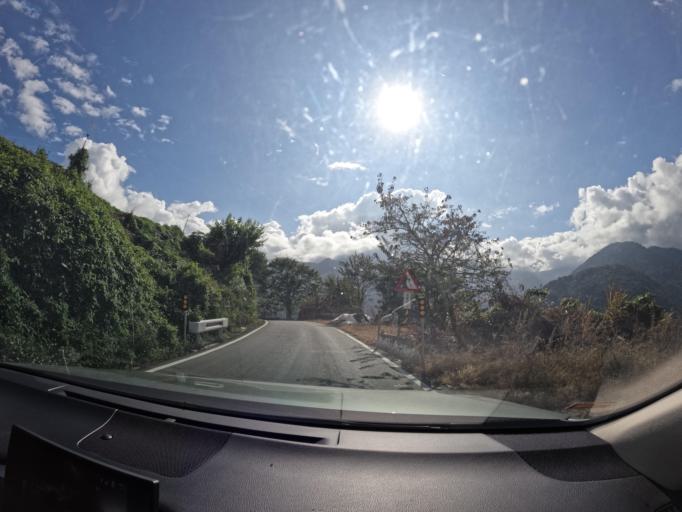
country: TW
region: Taiwan
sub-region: Taitung
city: Taitung
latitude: 23.1960
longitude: 121.0238
